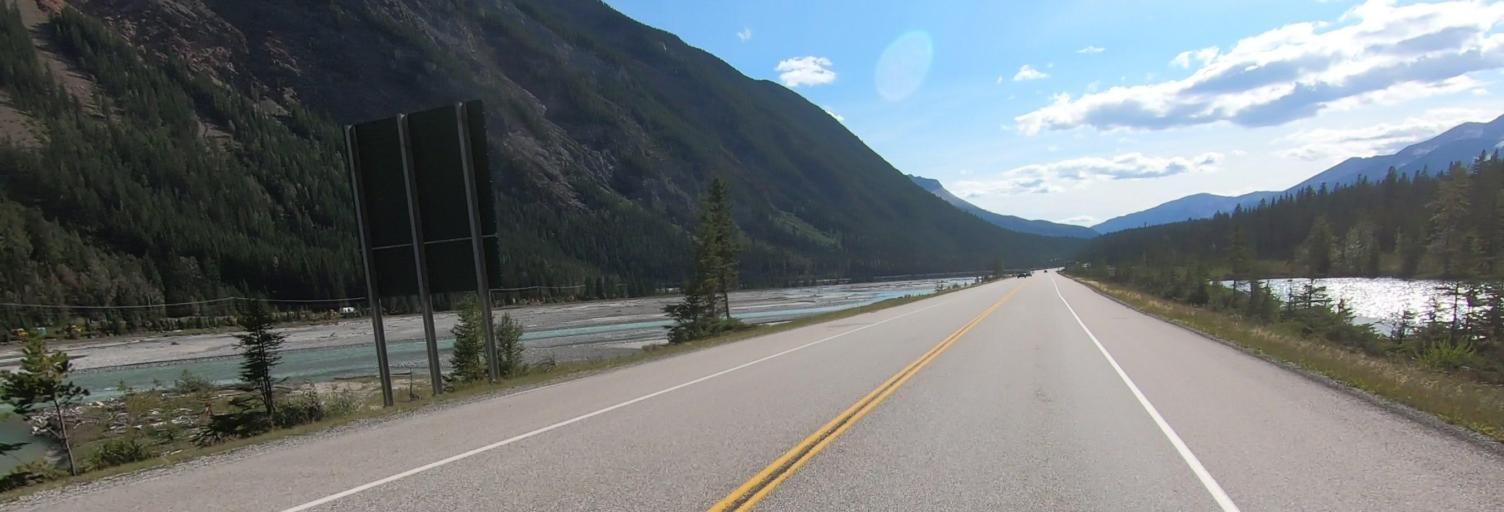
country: CA
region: Alberta
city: Lake Louise
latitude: 51.3908
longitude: -116.4987
